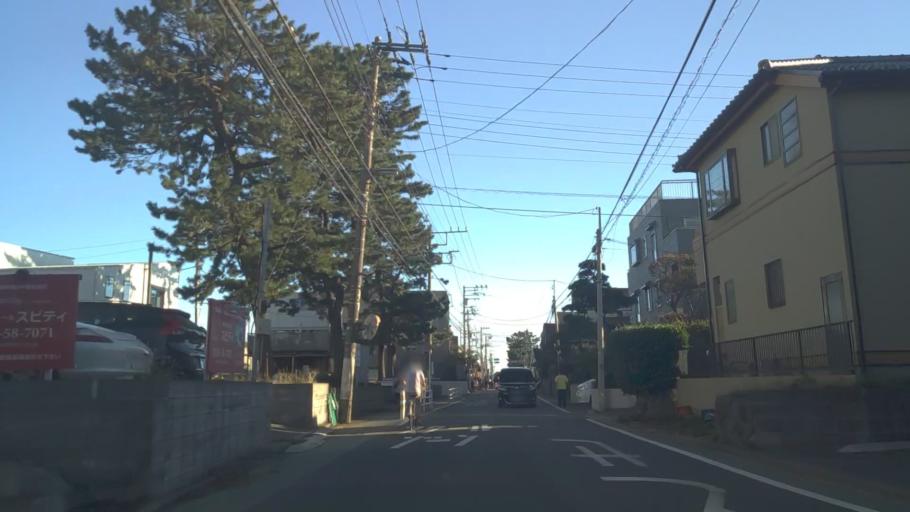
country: JP
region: Kanagawa
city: Chigasaki
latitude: 35.3221
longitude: 139.4154
